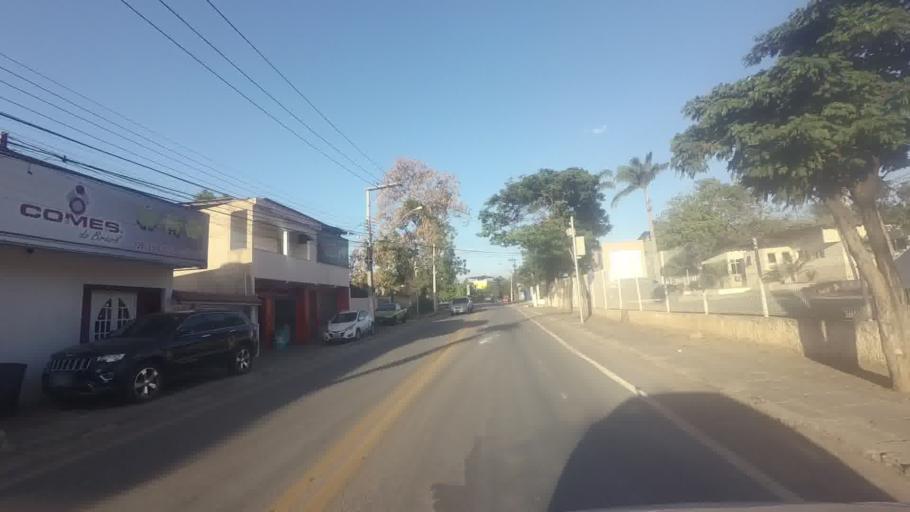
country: BR
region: Espirito Santo
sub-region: Cachoeiro De Itapemirim
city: Cachoeiro de Itapemirim
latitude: -20.8327
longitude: -41.1763
